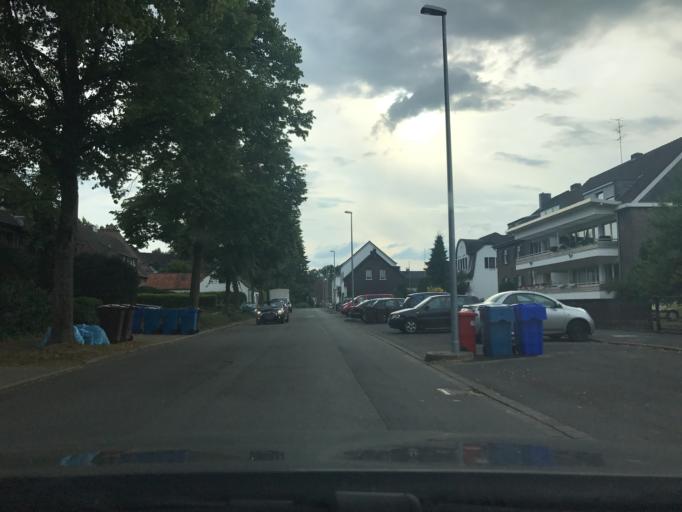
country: DE
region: North Rhine-Westphalia
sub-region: Regierungsbezirk Dusseldorf
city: Krefeld
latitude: 51.3611
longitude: 6.5804
